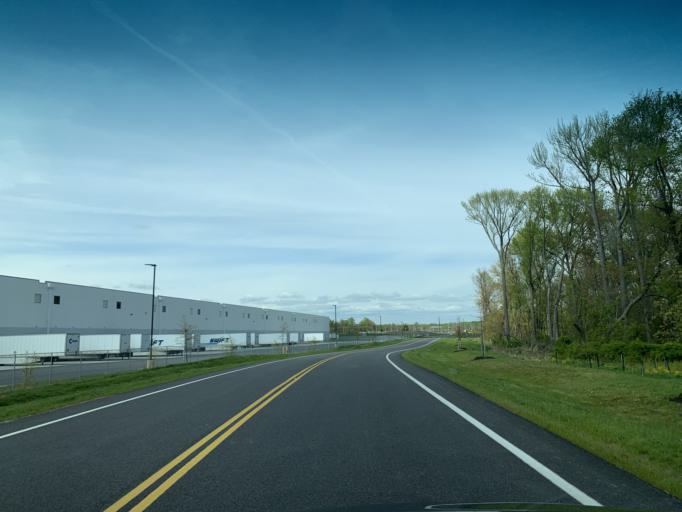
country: US
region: Maryland
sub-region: Harford County
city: Perryman
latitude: 39.4831
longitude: -76.1785
